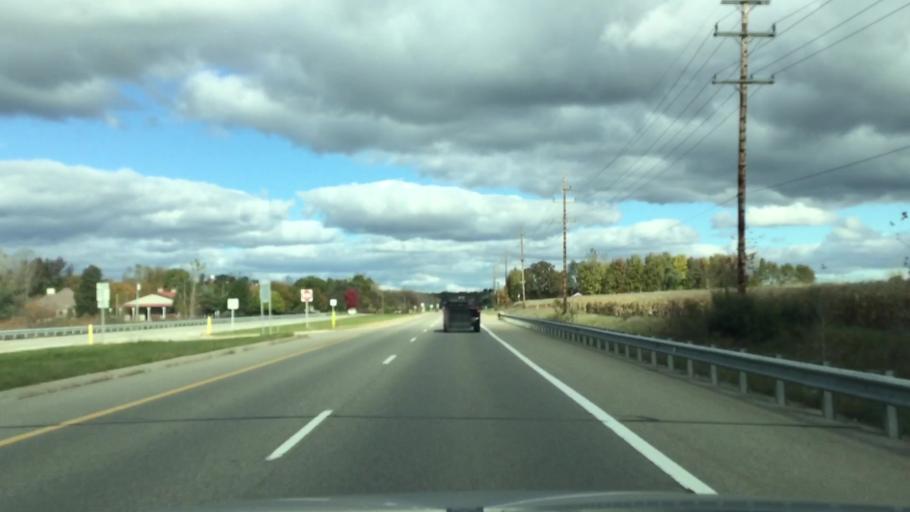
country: US
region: Michigan
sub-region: Lapeer County
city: Lapeer
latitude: 42.9799
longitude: -83.3152
